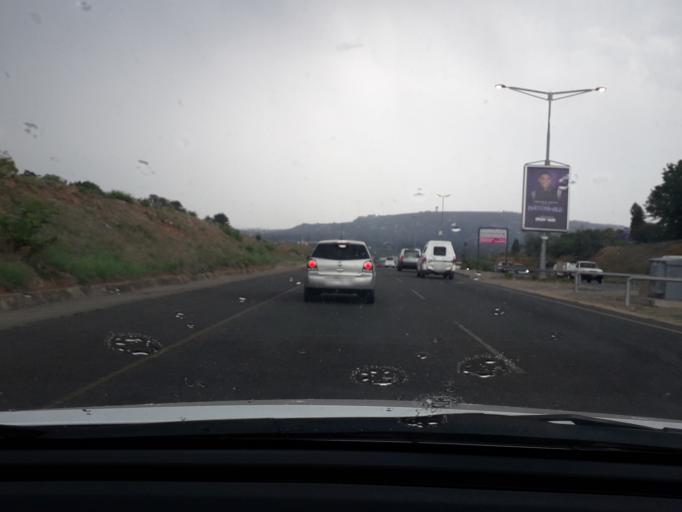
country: ZA
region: Gauteng
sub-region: City of Johannesburg Metropolitan Municipality
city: Roodepoort
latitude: -26.1092
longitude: 27.9501
